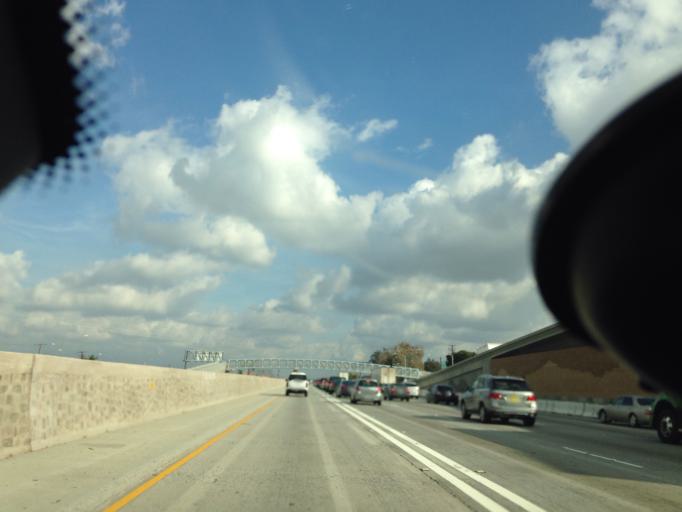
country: US
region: California
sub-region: Los Angeles County
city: West Puente Valley
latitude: 34.0660
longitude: -117.9927
